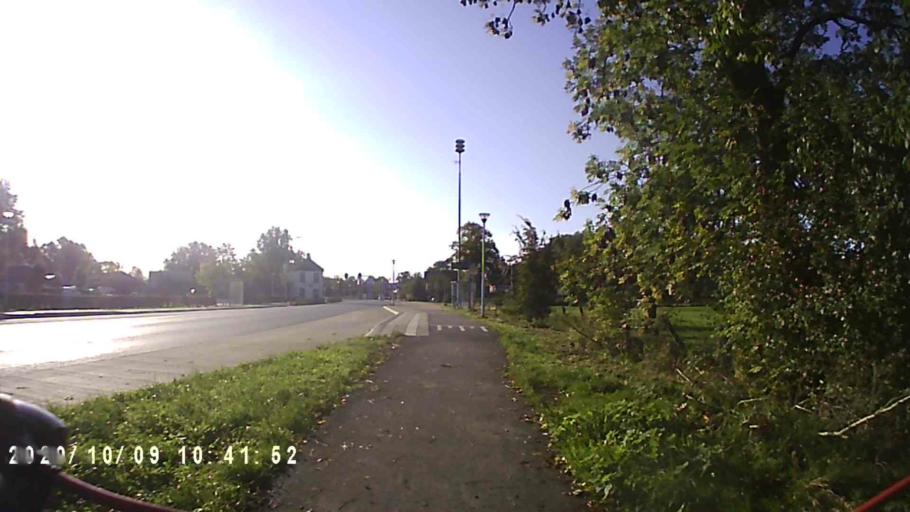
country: NL
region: Groningen
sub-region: Gemeente Groningen
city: Korrewegwijk
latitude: 53.2762
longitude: 6.5348
